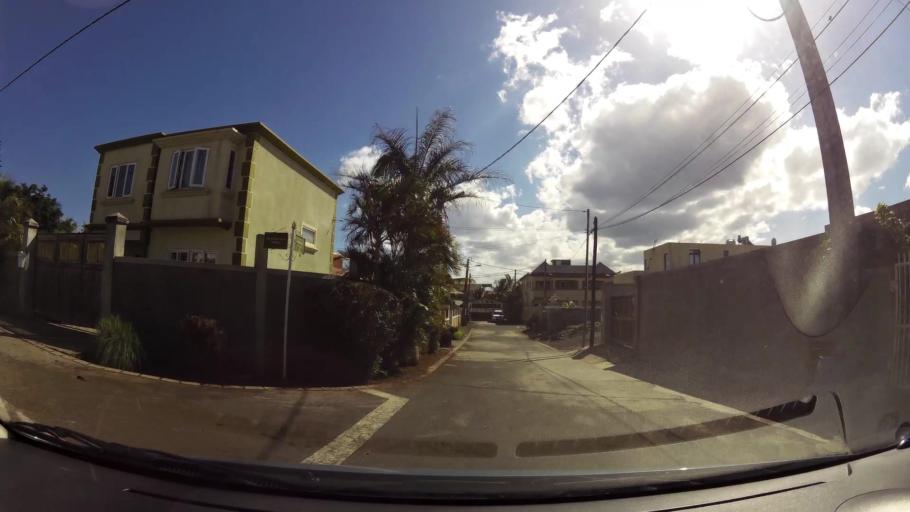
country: MU
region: Black River
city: Albion
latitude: -20.2252
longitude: 57.4141
